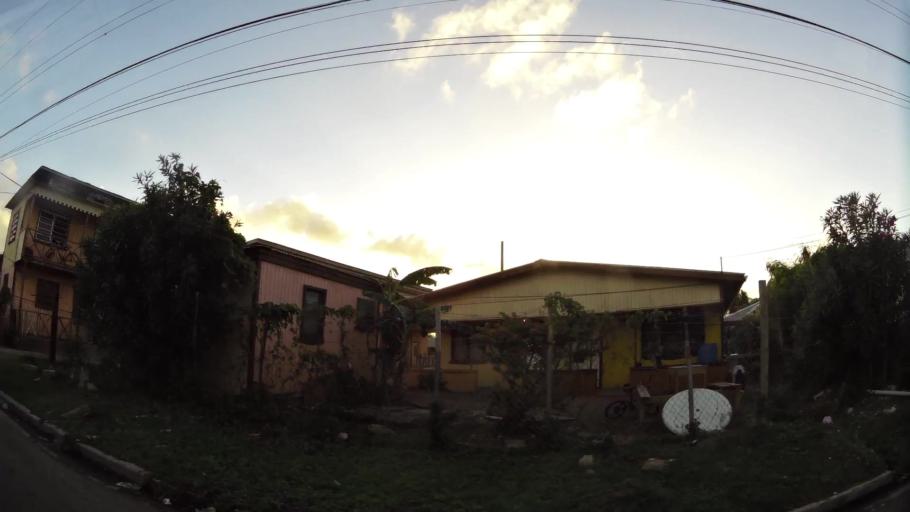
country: AG
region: Saint John
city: Saint John's
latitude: 17.1318
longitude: -61.8386
